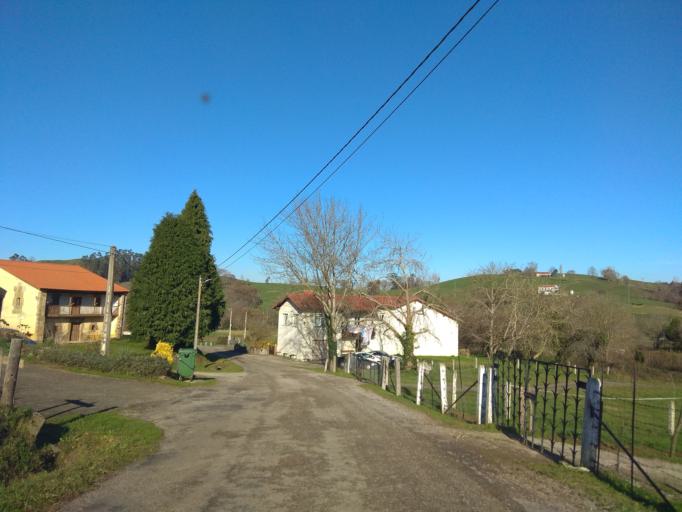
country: ES
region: Cantabria
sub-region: Provincia de Cantabria
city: Entrambasaguas
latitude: 43.3686
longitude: -3.6613
